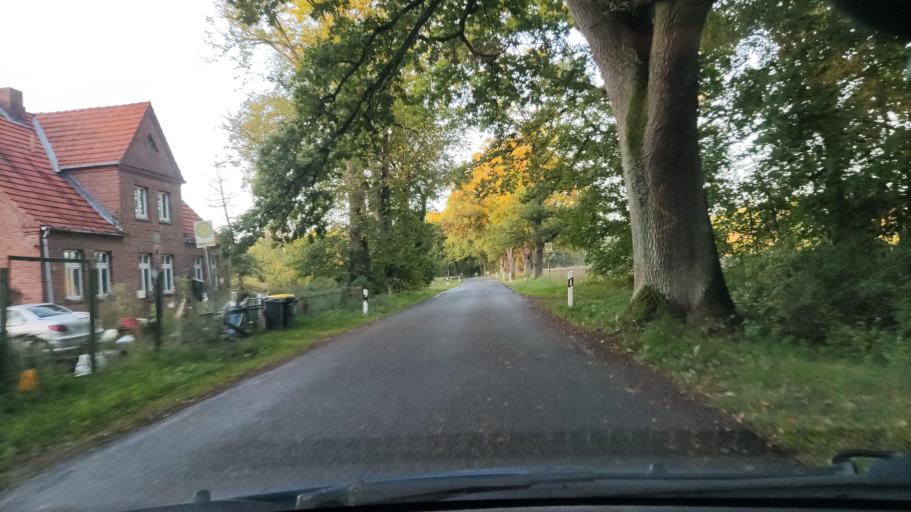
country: DE
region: Mecklenburg-Vorpommern
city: Lubtheen
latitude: 53.3048
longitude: 11.0054
